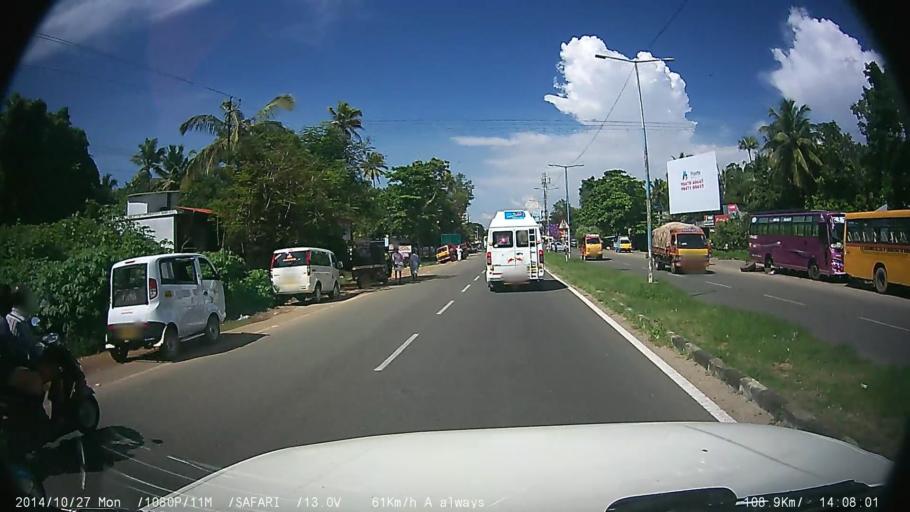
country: IN
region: Kerala
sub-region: Alappuzha
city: Kutiatodu
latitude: 9.7658
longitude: 76.3178
